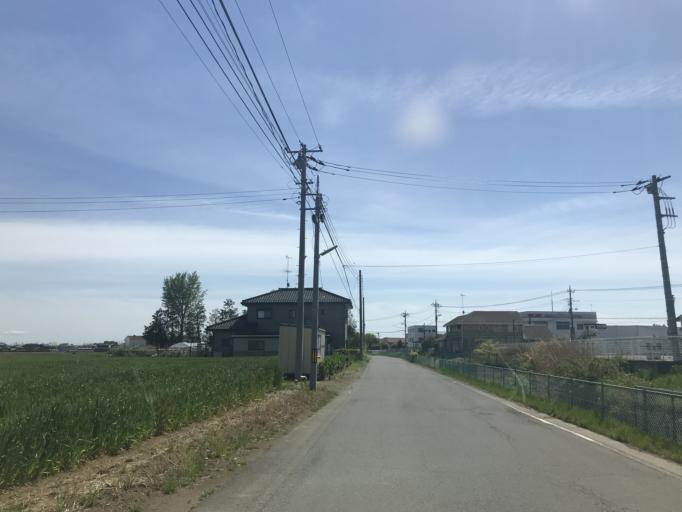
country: JP
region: Ibaraki
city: Mitsukaido
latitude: 36.0603
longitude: 139.9817
